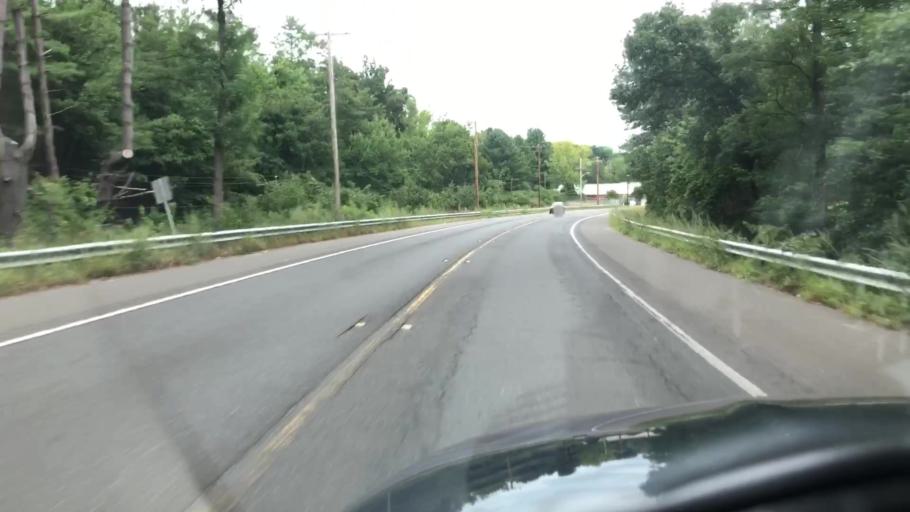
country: US
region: Massachusetts
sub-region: Hampshire County
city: Northampton
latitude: 42.3017
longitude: -72.6553
